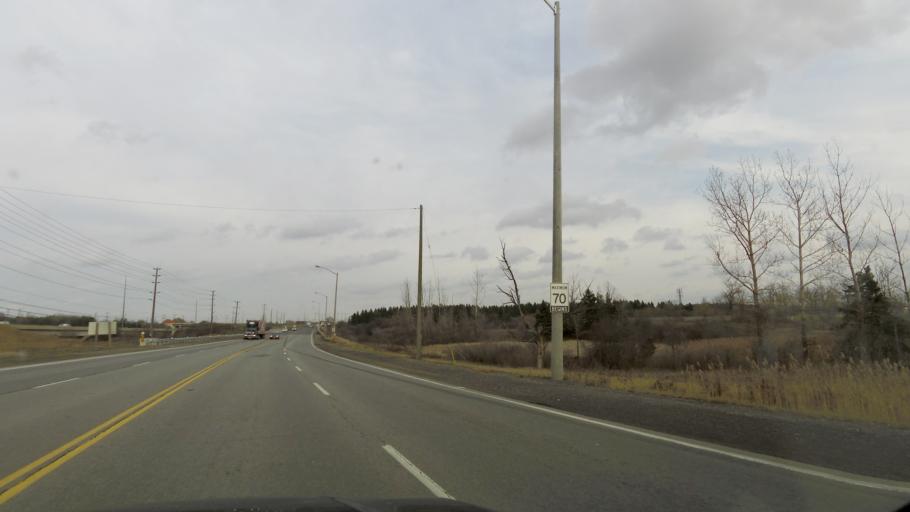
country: CA
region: Ontario
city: Etobicoke
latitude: 43.7458
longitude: -79.6443
